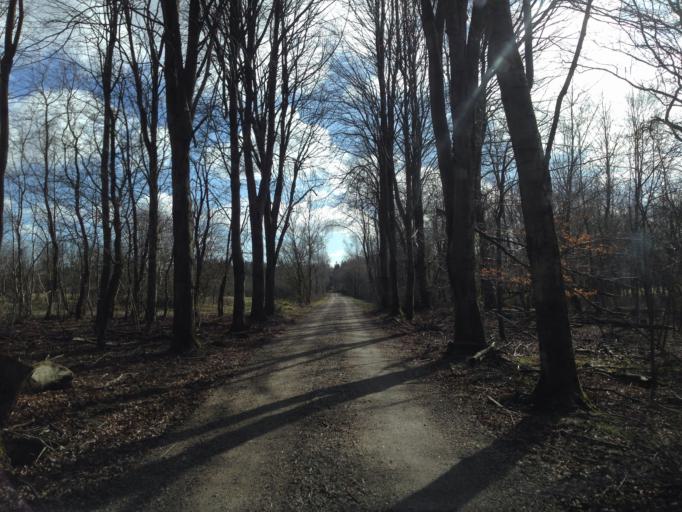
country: DK
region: Central Jutland
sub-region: Holstebro Kommune
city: Ulfborg
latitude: 56.2728
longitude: 8.4335
